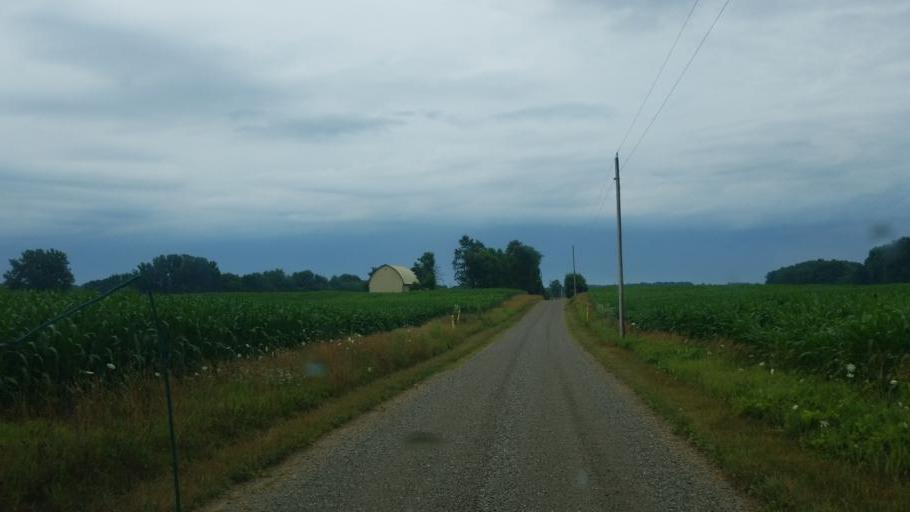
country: US
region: Indiana
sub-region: Steuben County
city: Hamilton
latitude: 41.5053
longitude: -84.9184
